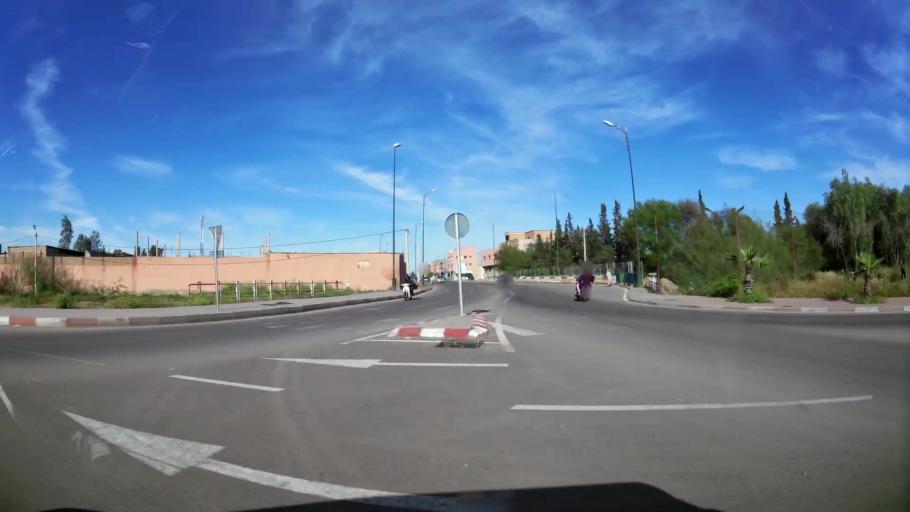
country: MA
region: Marrakech-Tensift-Al Haouz
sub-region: Marrakech
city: Marrakesh
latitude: 31.6798
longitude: -8.0537
